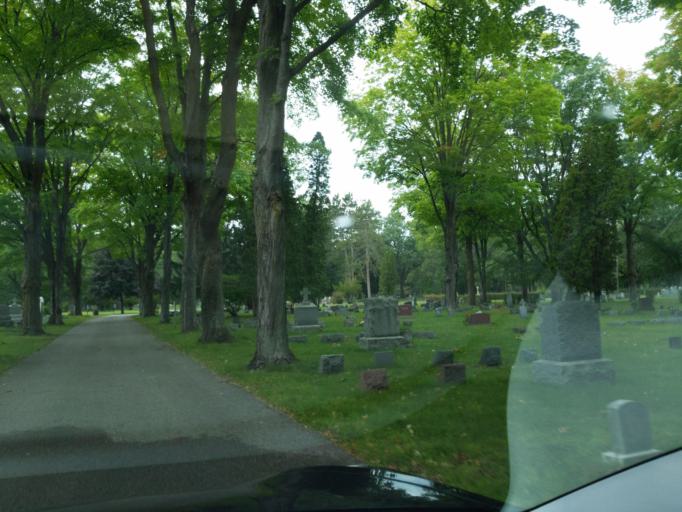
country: US
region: Michigan
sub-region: Grand Traverse County
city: Traverse City
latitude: 44.7555
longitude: -85.5867
